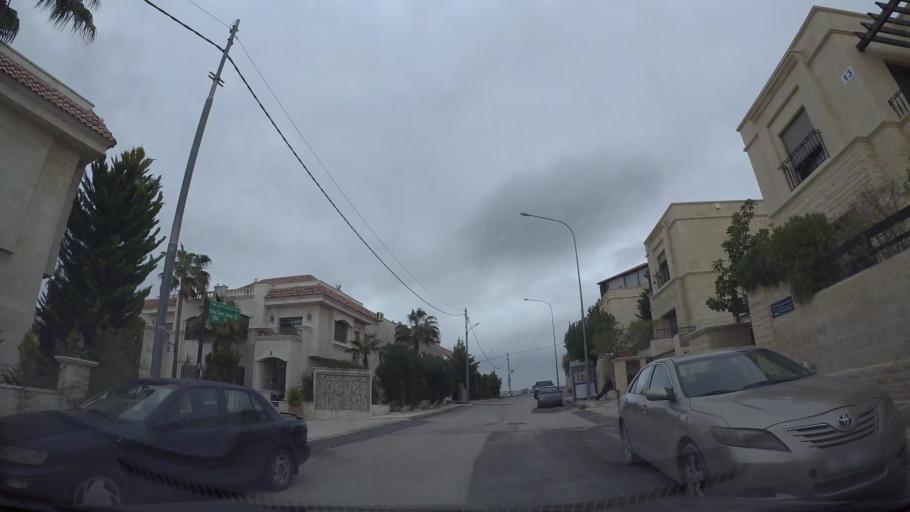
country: JO
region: Amman
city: Wadi as Sir
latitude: 31.9631
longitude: 35.8210
